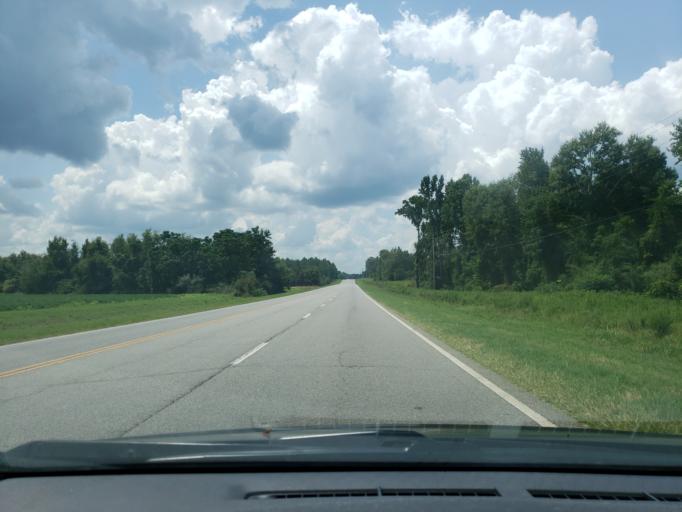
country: US
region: Georgia
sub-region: Pulaski County
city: Hawkinsville
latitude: 32.3207
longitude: -83.4171
